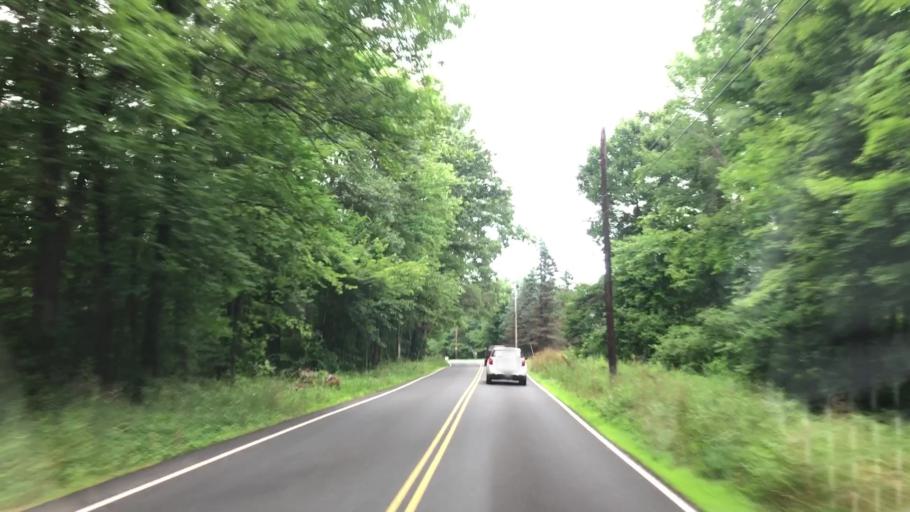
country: US
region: Massachusetts
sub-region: Hampshire County
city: Southampton
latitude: 42.2000
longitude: -72.7442
